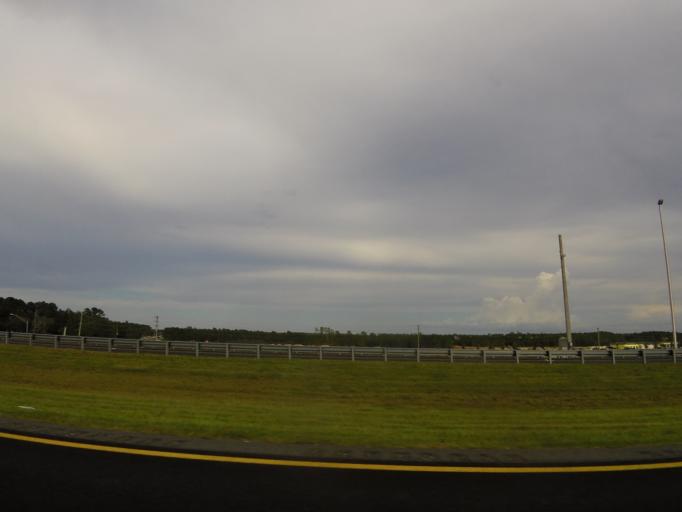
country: US
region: Florida
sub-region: Clay County
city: Middleburg
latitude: 30.1140
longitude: -81.8327
